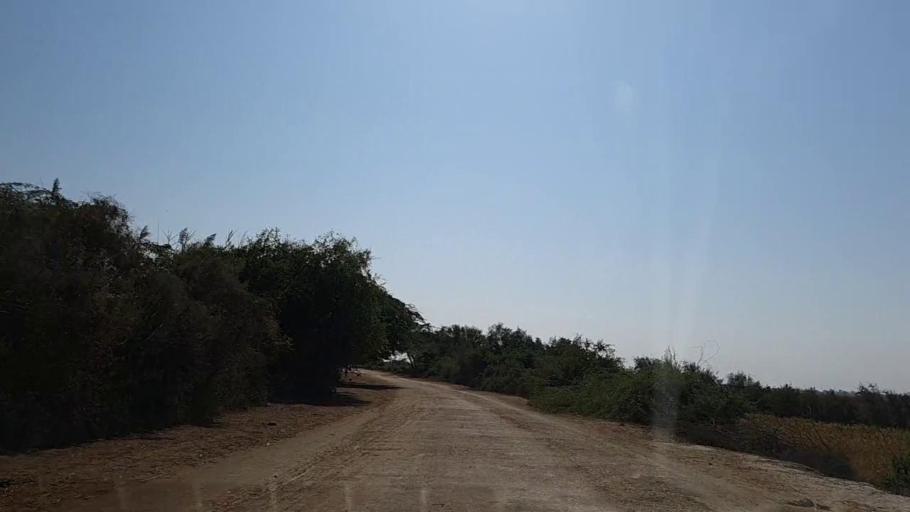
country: PK
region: Sindh
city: Chuhar Jamali
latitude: 24.5140
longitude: 68.0959
